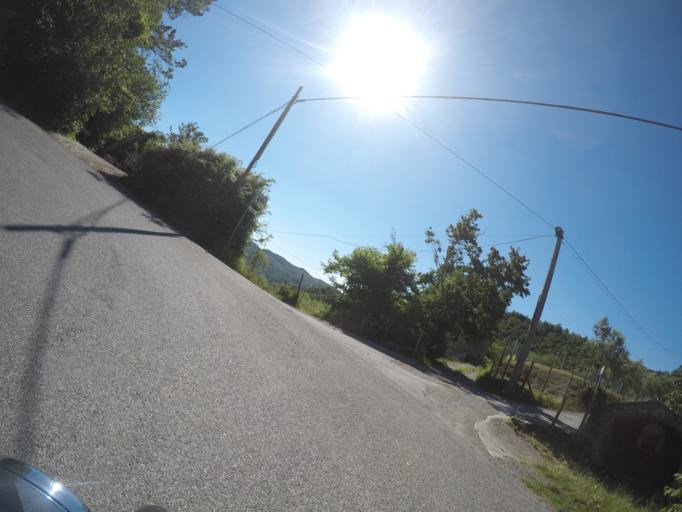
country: IT
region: Tuscany
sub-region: Provincia di Massa-Carrara
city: Fosdinovo
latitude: 44.1440
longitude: 10.0731
